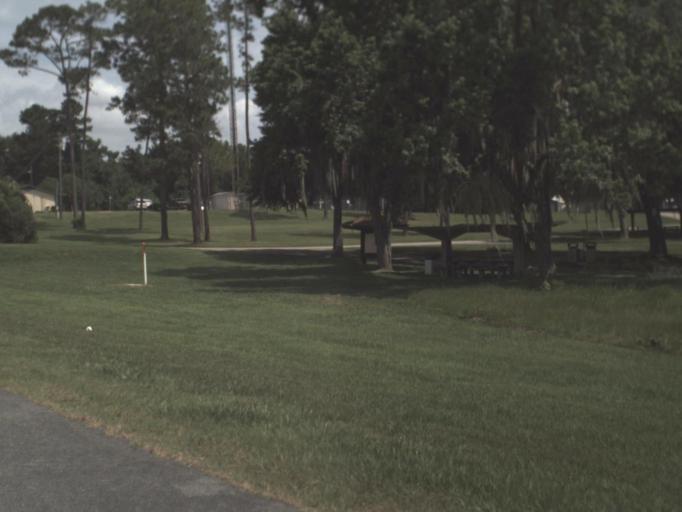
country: US
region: Florida
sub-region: Madison County
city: Madison
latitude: 30.4805
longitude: -83.4479
